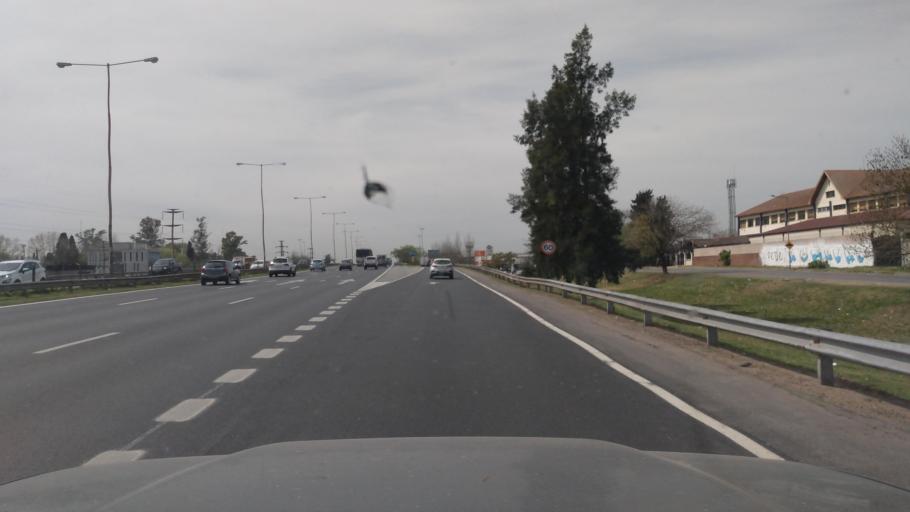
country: AR
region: Buenos Aires
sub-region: Partido de Pilar
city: Pilar
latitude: -34.4503
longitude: -58.9091
